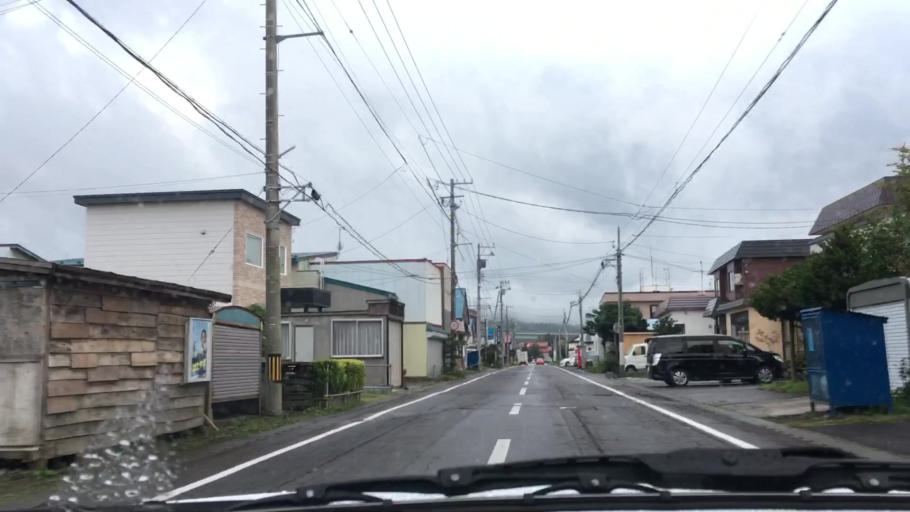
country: JP
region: Hokkaido
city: Nanae
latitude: 42.1893
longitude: 140.4257
